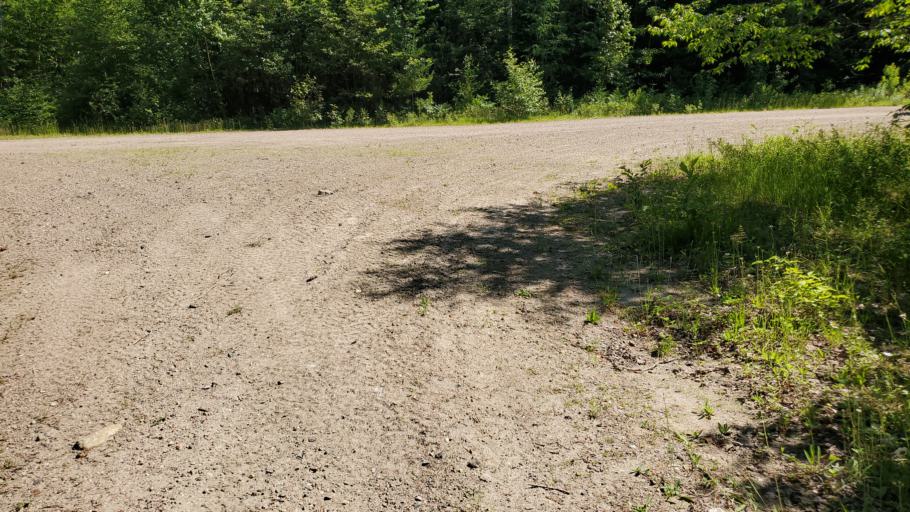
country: CA
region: Ontario
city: Mattawa
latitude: 46.2610
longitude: -78.2739
